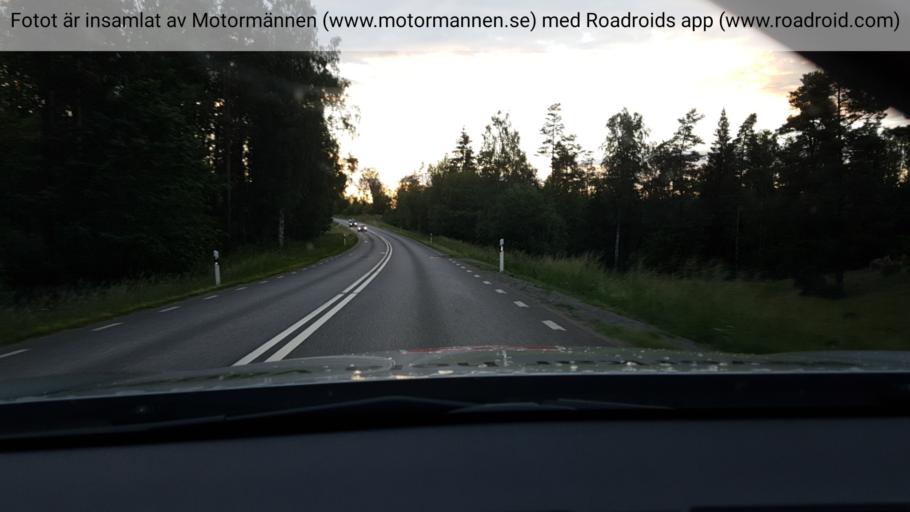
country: SE
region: Joenkoeping
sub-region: Mullsjo Kommun
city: Mullsjoe
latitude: 58.0678
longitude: 13.8075
